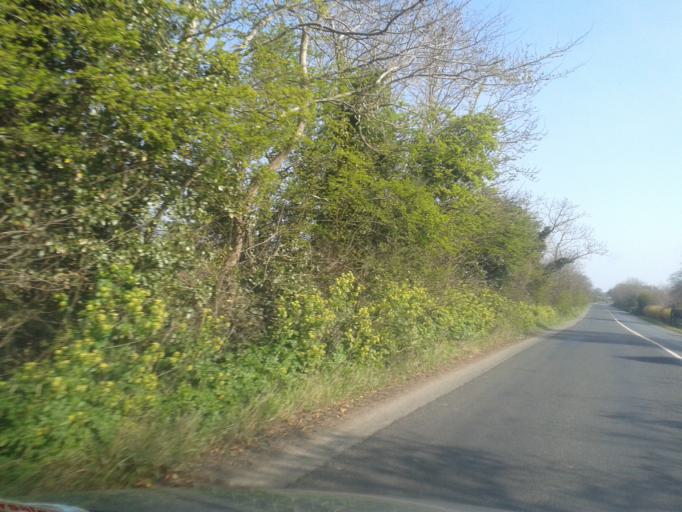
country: IE
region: Leinster
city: Balrothery
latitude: 53.5773
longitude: -6.2016
